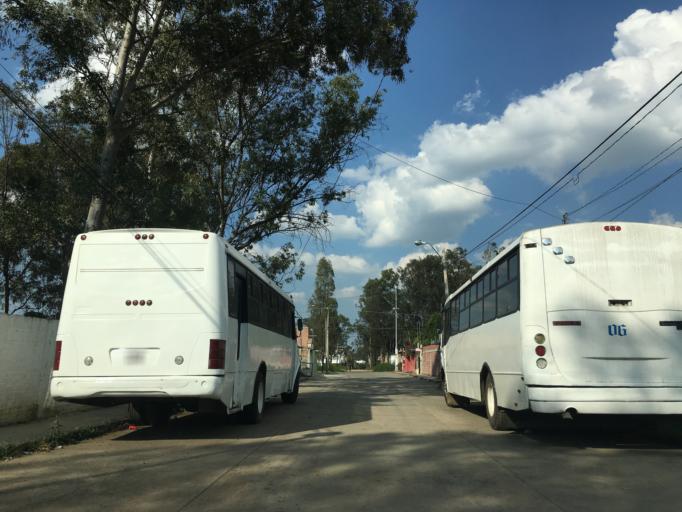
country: MX
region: Michoacan
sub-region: Morelia
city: Morelos
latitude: 19.6391
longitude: -101.2320
